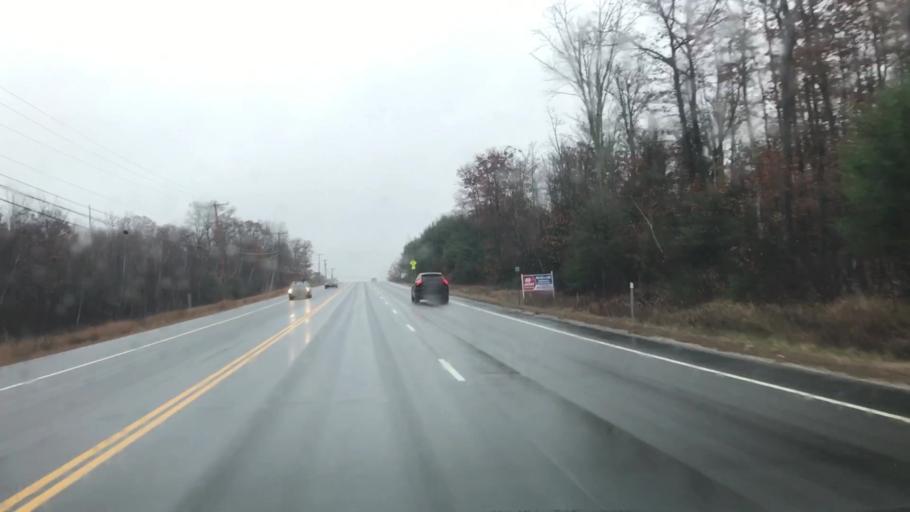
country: US
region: New Hampshire
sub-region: Merrimack County
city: Chichester
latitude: 43.2466
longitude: -71.4298
